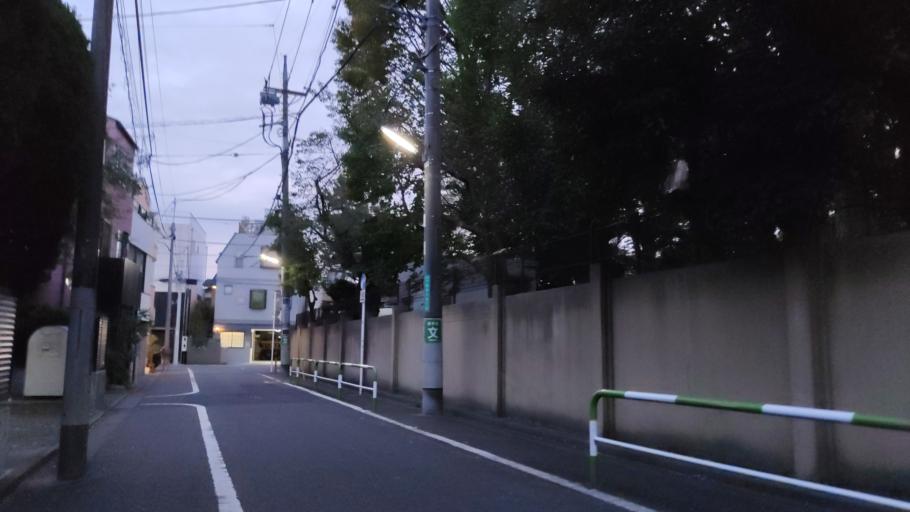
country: JP
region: Tokyo
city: Tokyo
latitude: 35.6349
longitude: 139.6790
